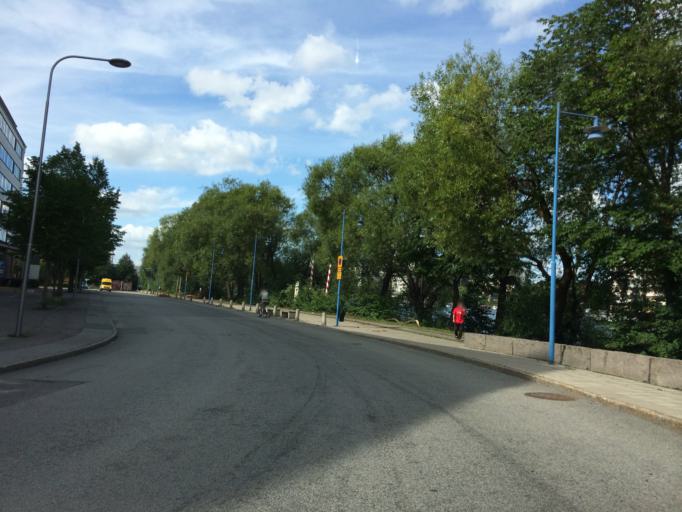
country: SE
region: Stockholm
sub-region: Stockholms Kommun
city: Arsta
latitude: 59.3138
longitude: 18.0290
